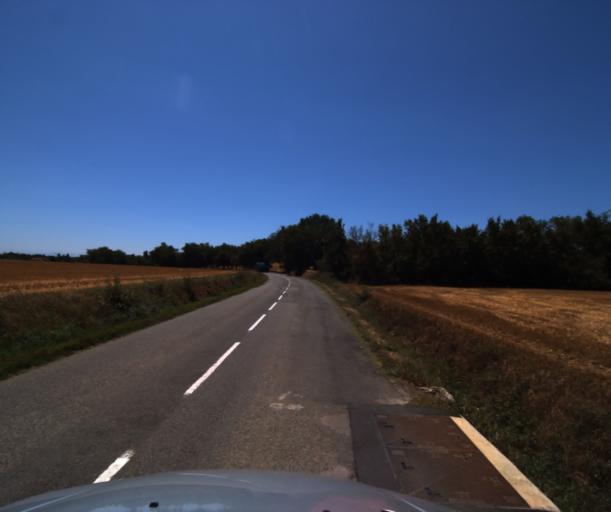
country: FR
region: Midi-Pyrenees
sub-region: Departement de la Haute-Garonne
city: Muret
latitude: 43.4674
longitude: 1.3490
